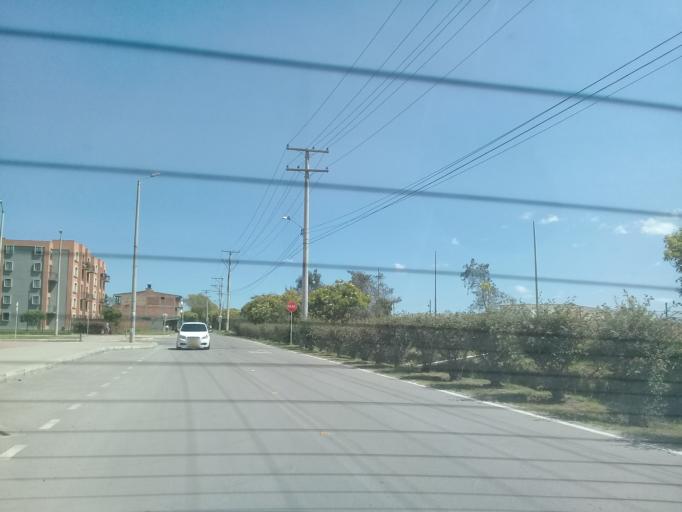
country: CO
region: Cundinamarca
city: Madrid
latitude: 4.7232
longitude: -74.2478
